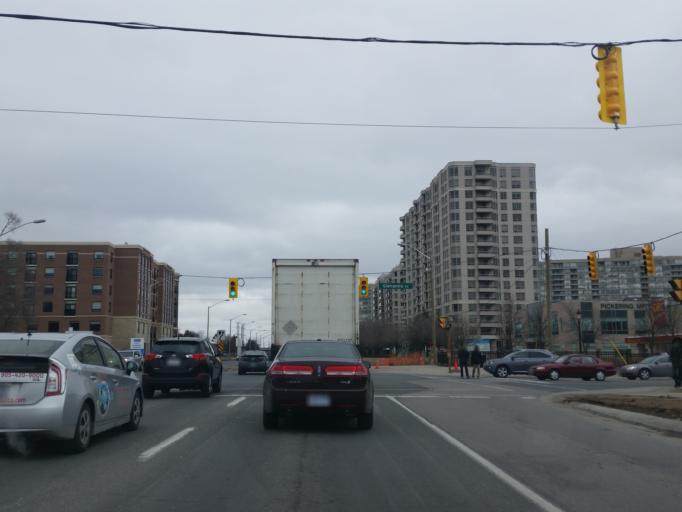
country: CA
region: Ontario
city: Ajax
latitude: 43.8381
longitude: -79.0871
